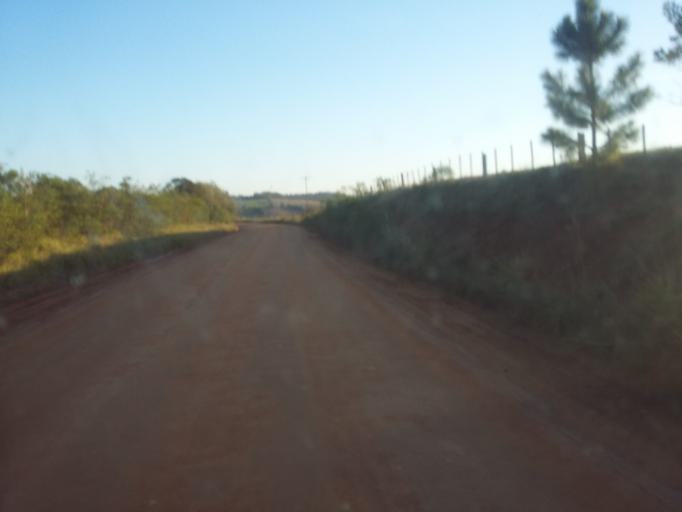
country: BR
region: Rio Grande do Sul
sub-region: Camaqua
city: Camaqua
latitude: -30.7595
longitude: -51.7811
